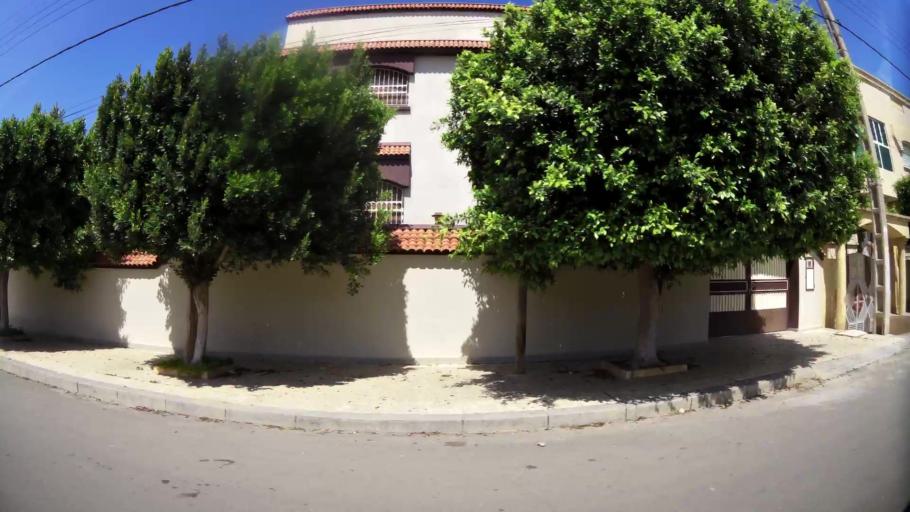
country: MA
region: Oriental
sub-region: Oujda-Angad
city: Oujda
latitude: 34.6868
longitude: -1.8783
